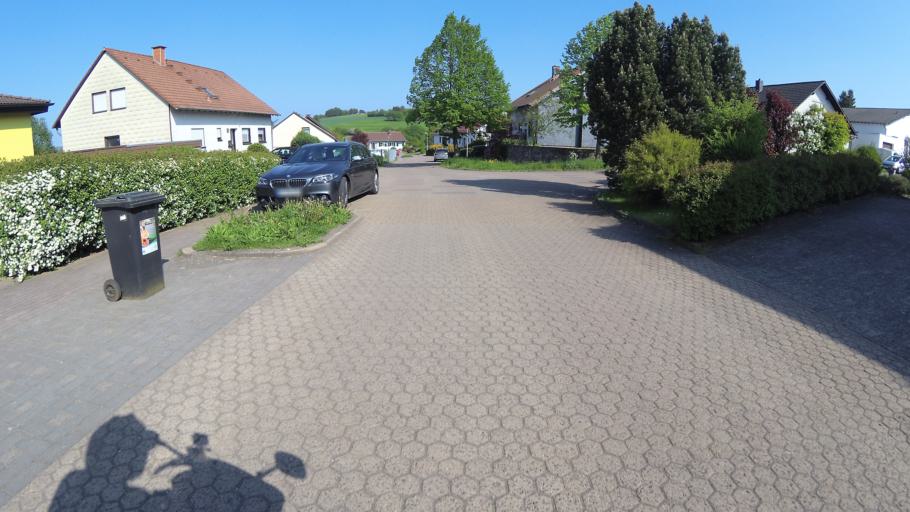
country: DE
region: Saarland
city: Illingen
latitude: 49.3668
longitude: 7.0462
